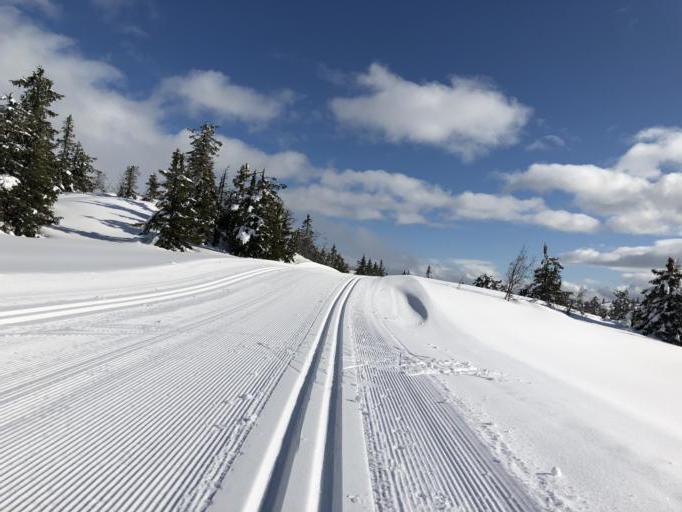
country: NO
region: Oppland
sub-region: Gausdal
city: Segalstad bru
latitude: 61.3322
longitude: 10.0301
